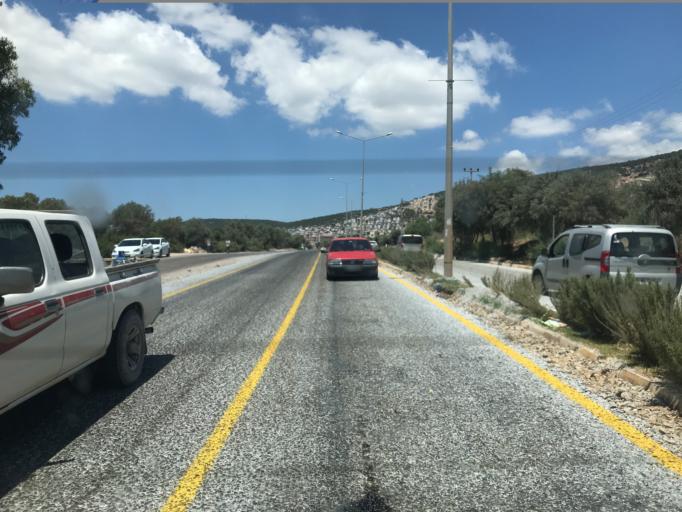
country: TR
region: Aydin
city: Sarikemer
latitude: 37.4135
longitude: 27.4221
